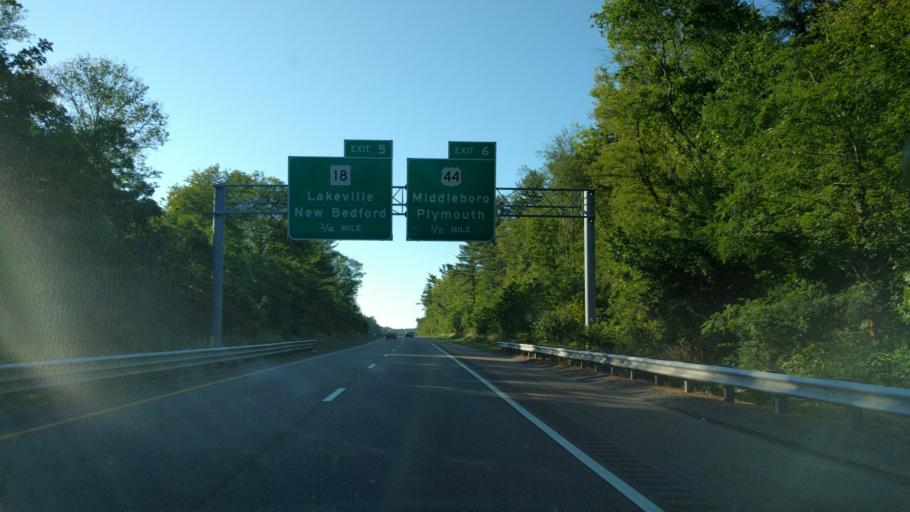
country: US
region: Massachusetts
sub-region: Plymouth County
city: Middleborough Center
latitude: 41.9081
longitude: -70.9735
